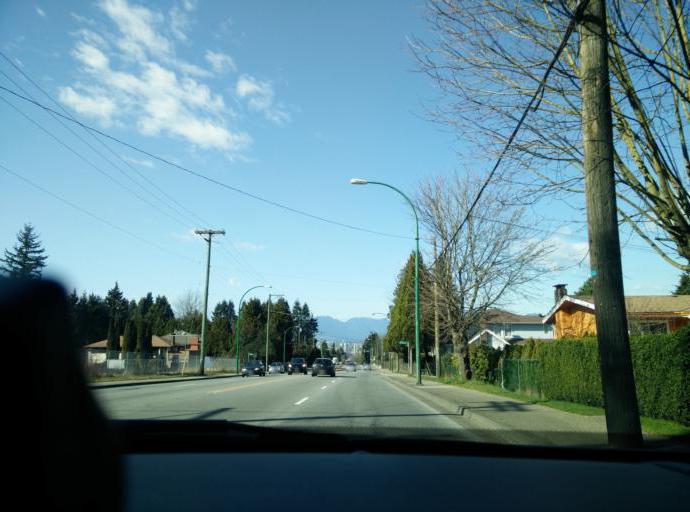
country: CA
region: British Columbia
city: Burnaby
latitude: 49.2274
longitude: -122.9450
